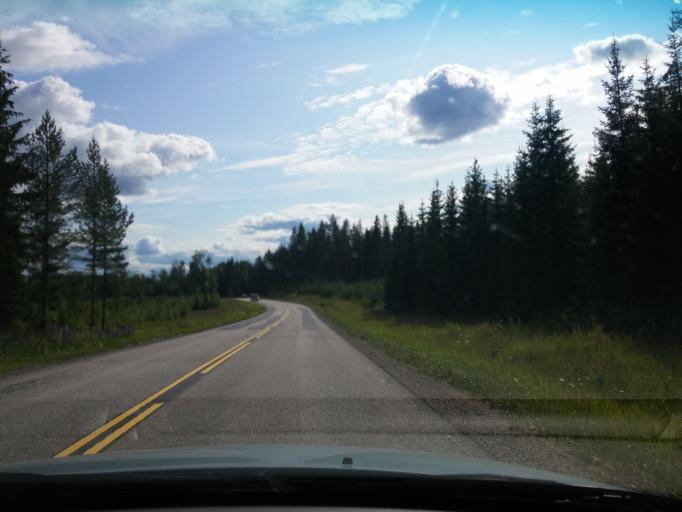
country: FI
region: Central Finland
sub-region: Keuruu
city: Keuruu
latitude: 62.3214
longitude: 24.7326
